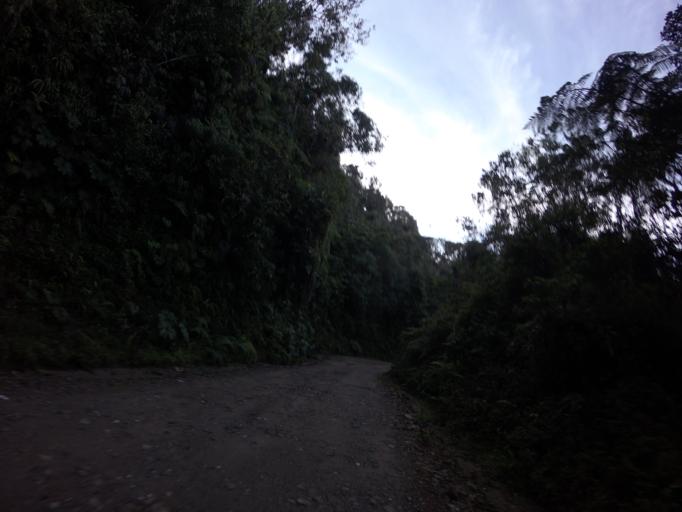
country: CO
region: Caldas
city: Pensilvania
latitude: 5.4129
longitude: -75.1315
